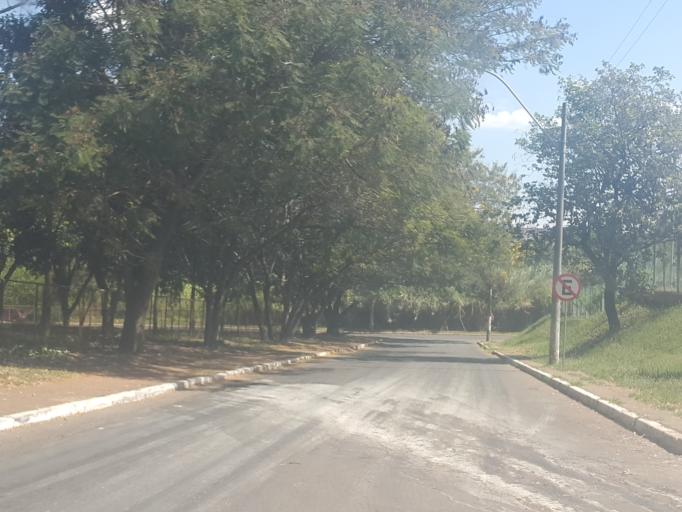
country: BR
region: Federal District
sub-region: Brasilia
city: Brasilia
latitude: -15.8212
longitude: -48.0700
